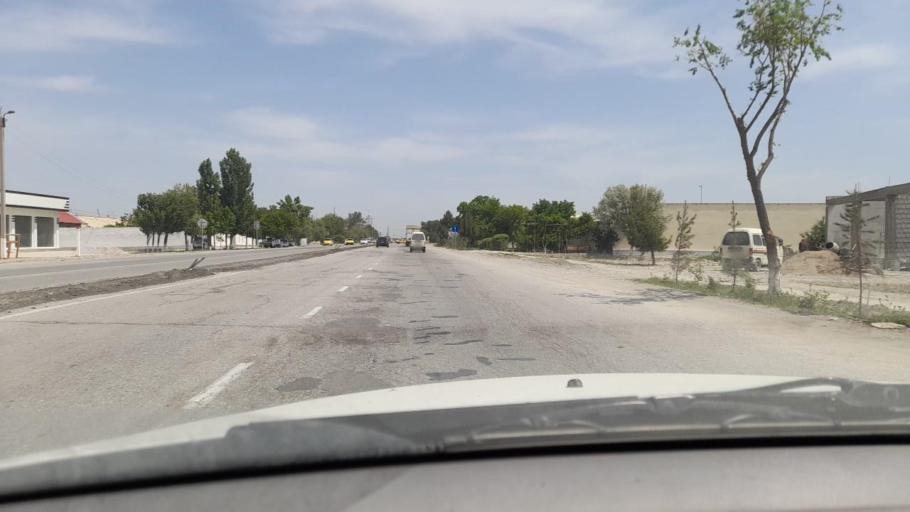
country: UZ
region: Navoiy
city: Beshrabot
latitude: 40.1448
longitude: 65.3036
